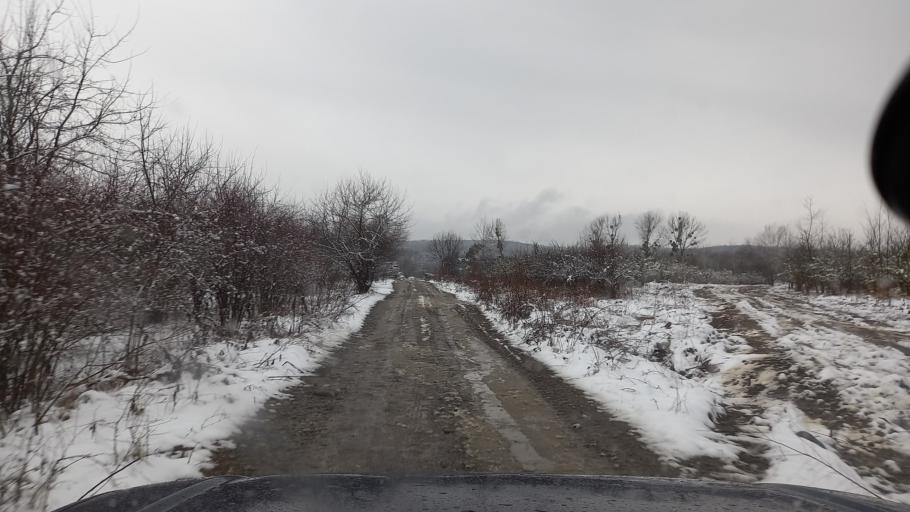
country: RU
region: Adygeya
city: Abadzekhskaya
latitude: 44.3731
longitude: 40.2518
